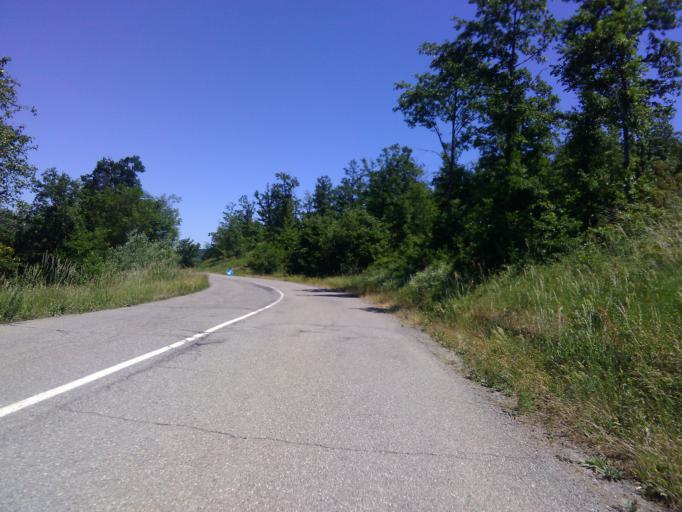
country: IT
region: Emilia-Romagna
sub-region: Provincia di Parma
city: Berceto
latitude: 44.5600
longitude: 10.0376
